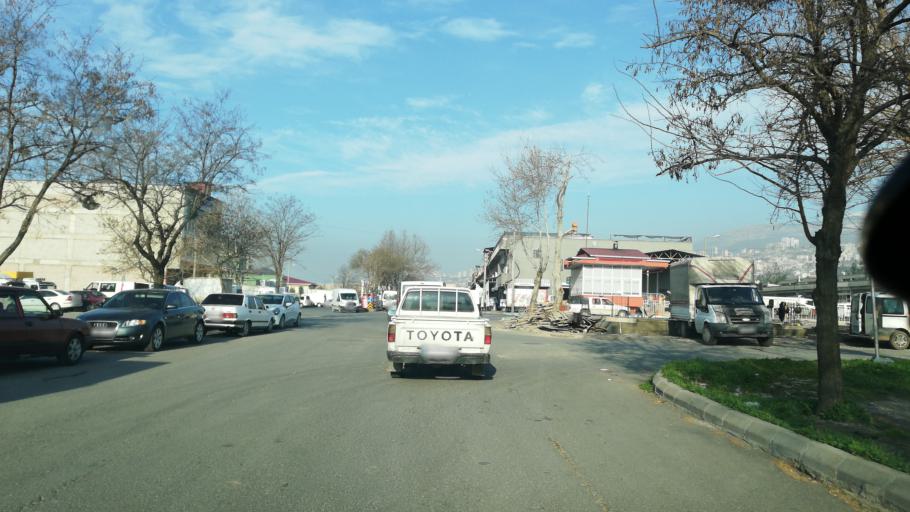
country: TR
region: Kahramanmaras
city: Kahramanmaras
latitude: 37.5639
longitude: 36.9224
